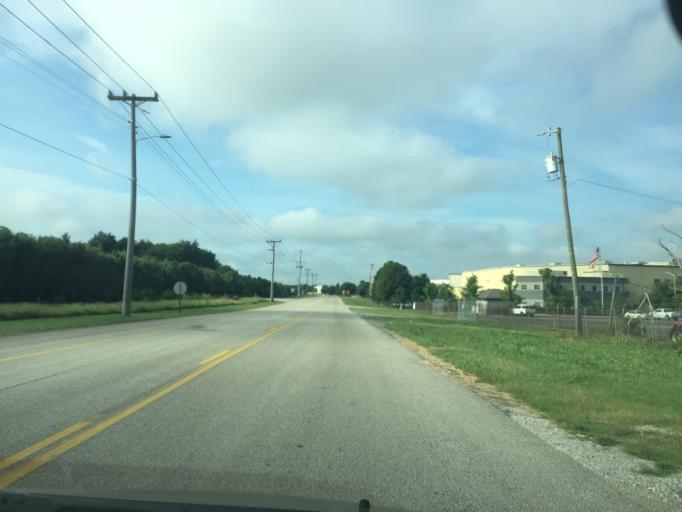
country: US
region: Tennessee
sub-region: Hamilton County
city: East Chattanooga
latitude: 35.0809
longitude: -85.2707
